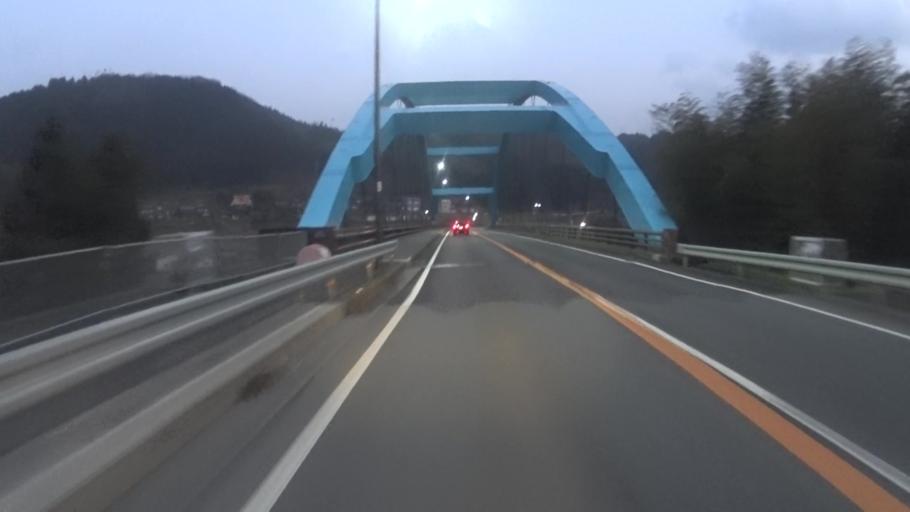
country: JP
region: Kyoto
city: Ayabe
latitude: 35.2700
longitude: 135.3957
